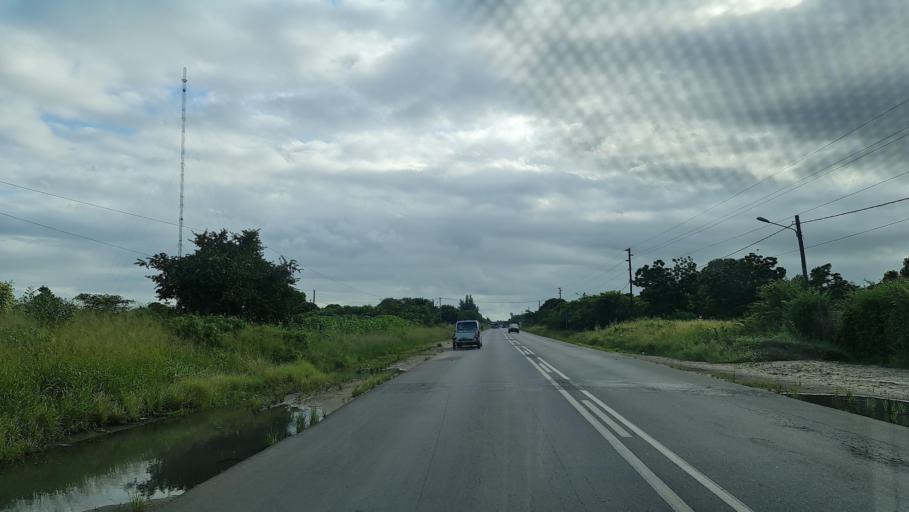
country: MZ
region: Maputo
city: Manhica
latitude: -25.4181
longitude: 32.7322
